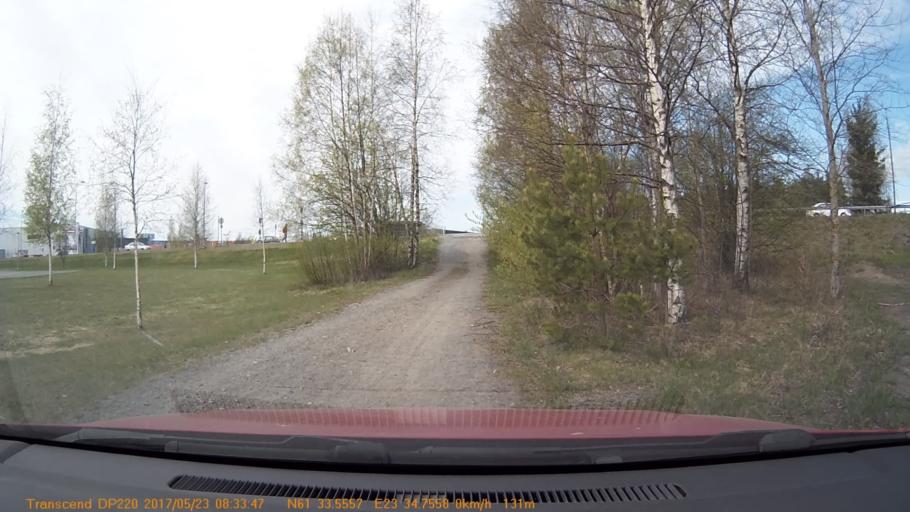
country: FI
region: Pirkanmaa
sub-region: Tampere
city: Yloejaervi
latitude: 61.5593
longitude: 23.5793
